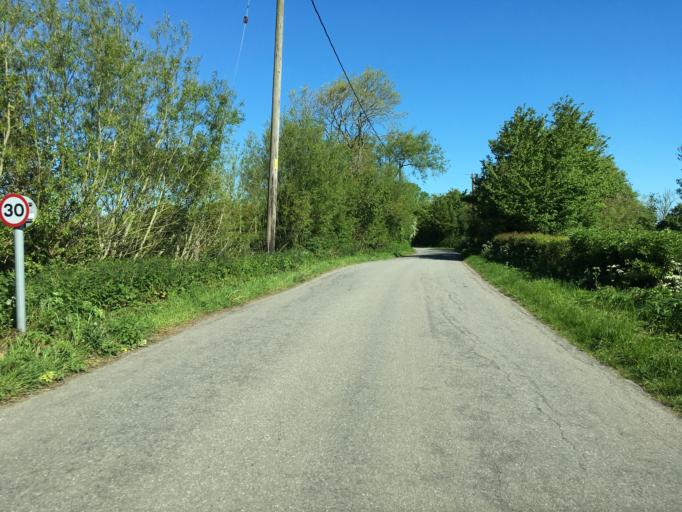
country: GB
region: England
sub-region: South Gloucestershire
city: Severn Beach
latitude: 51.5761
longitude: -2.6355
